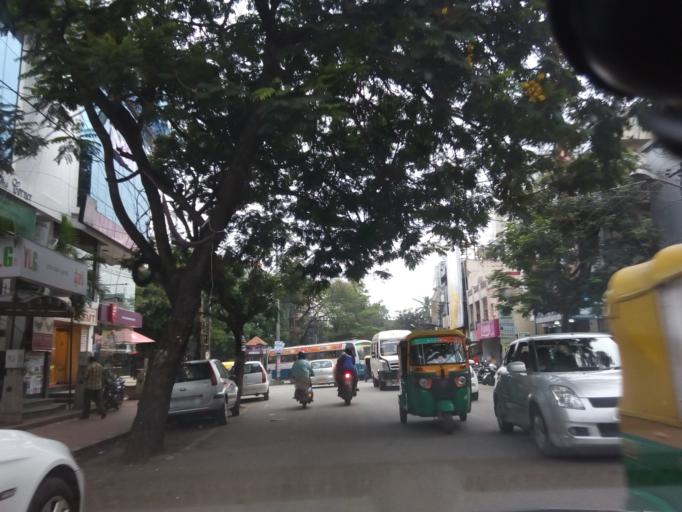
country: IN
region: Karnataka
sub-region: Bangalore Urban
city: Bangalore
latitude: 12.9961
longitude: 77.6130
